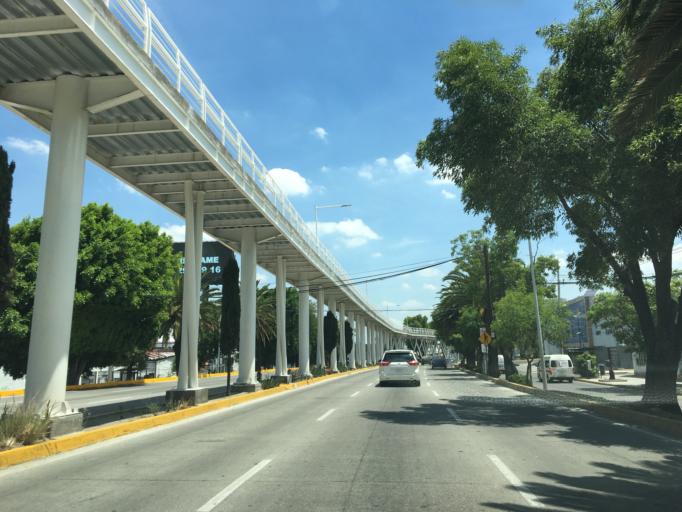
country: MX
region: Puebla
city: Puebla
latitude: 19.0720
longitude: -98.2268
